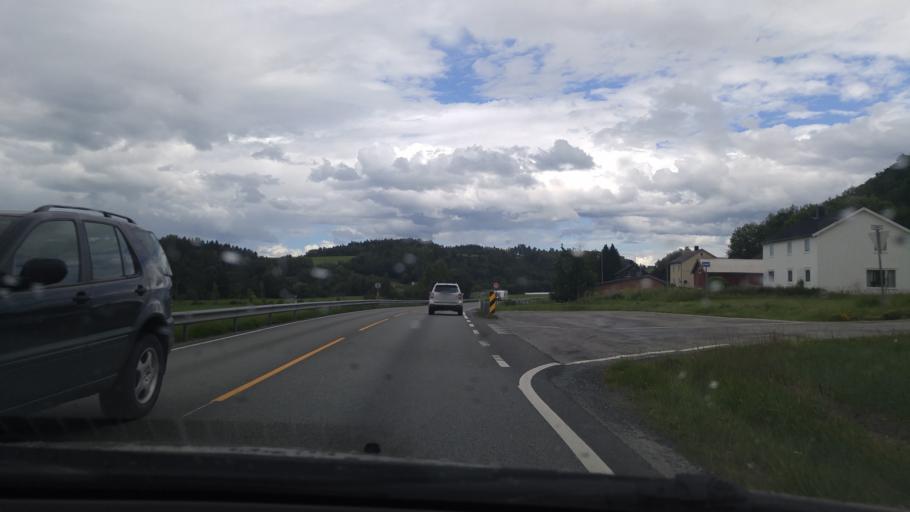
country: NO
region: Nord-Trondelag
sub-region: Inderoy
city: Straumen
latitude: 63.8703
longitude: 11.4041
